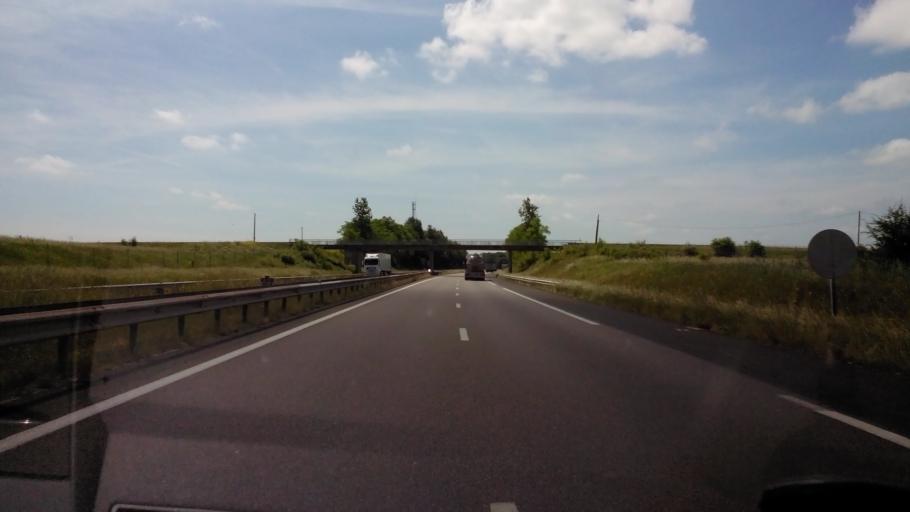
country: FR
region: Lorraine
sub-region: Departement des Vosges
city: Chatenois
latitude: 48.2596
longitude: 5.8650
